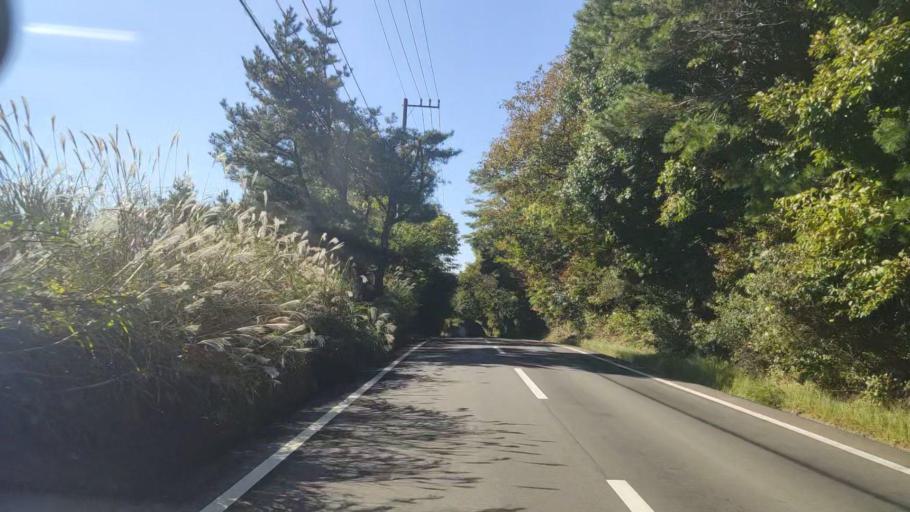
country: JP
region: Shizuoka
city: Atami
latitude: 35.0372
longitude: 139.0185
